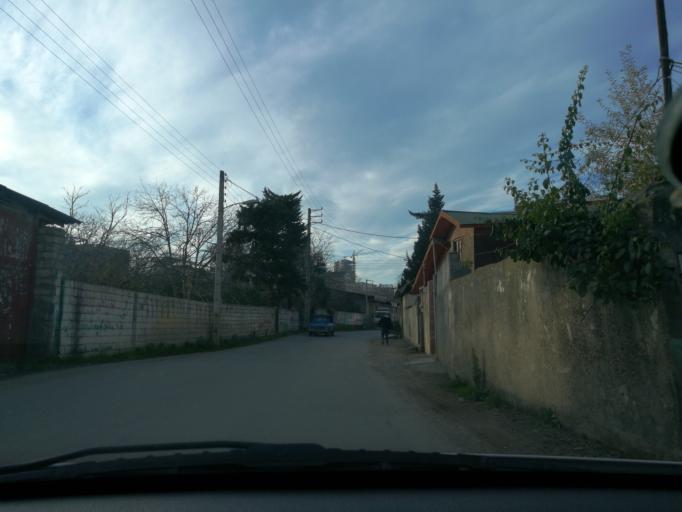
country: IR
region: Mazandaran
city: Chalus
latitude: 36.6446
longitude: 51.4327
